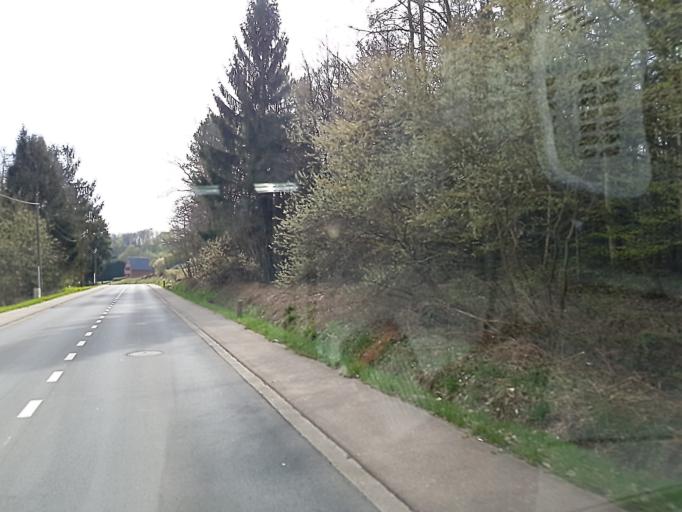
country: BE
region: Flanders
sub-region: Provincie Vlaams-Brabant
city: Diest
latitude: 50.9874
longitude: 5.0105
